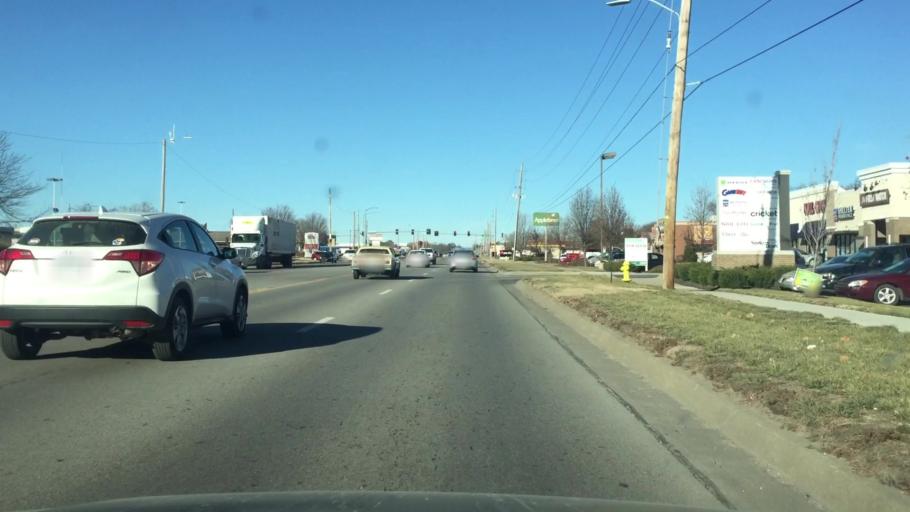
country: US
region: Kansas
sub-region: Douglas County
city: Lawrence
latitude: 38.9366
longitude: -95.2605
